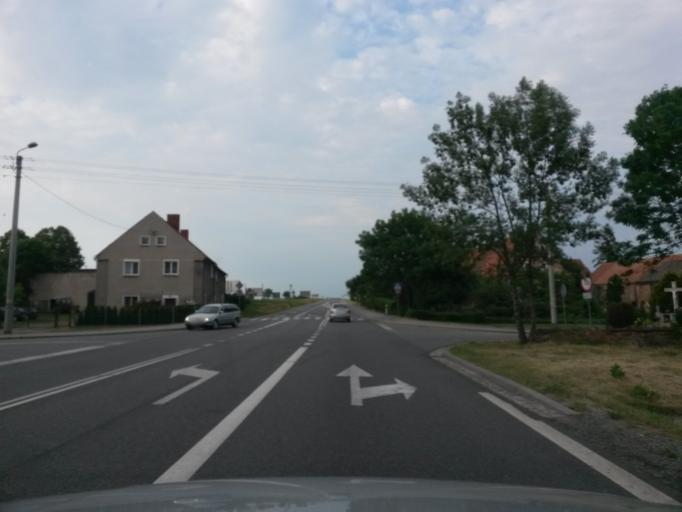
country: PL
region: Lower Silesian Voivodeship
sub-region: Powiat swidnicki
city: Zarow
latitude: 51.0084
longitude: 16.5476
